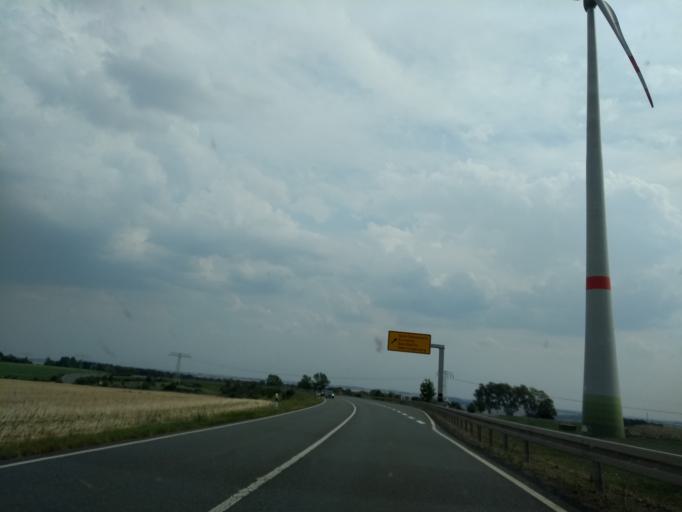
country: DE
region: Thuringia
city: Schwaara
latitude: 50.9409
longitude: 12.1111
